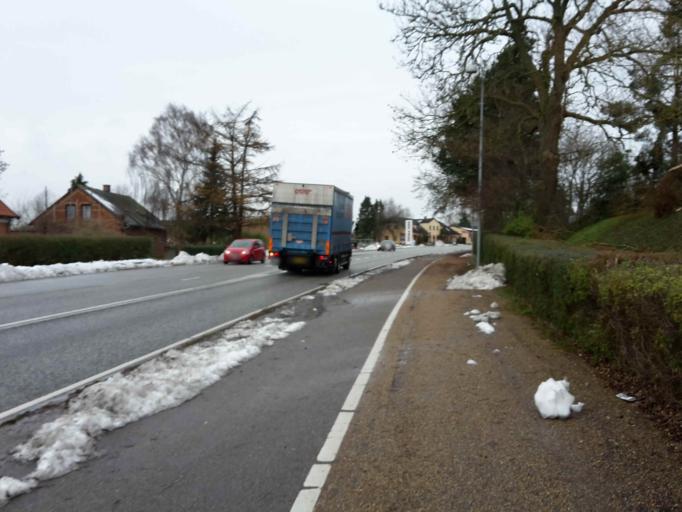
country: DK
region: Capital Region
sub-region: Allerod Kommune
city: Blovstrod
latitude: 55.8639
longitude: 12.3873
